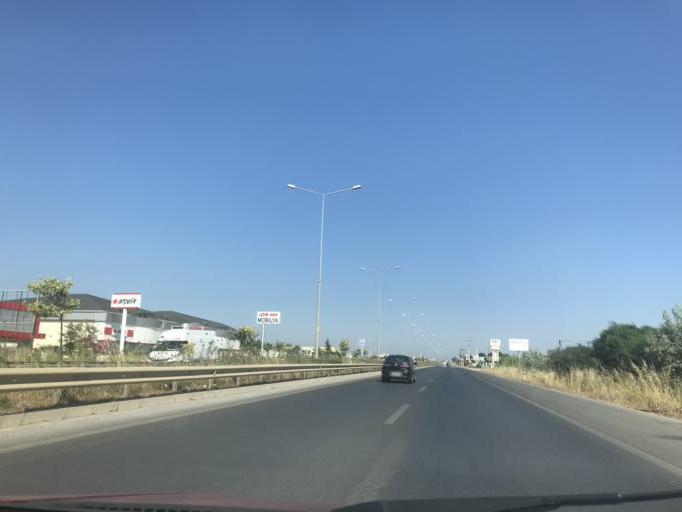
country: TR
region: Antalya
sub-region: Manavgat
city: Side
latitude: 36.8106
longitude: 31.3778
